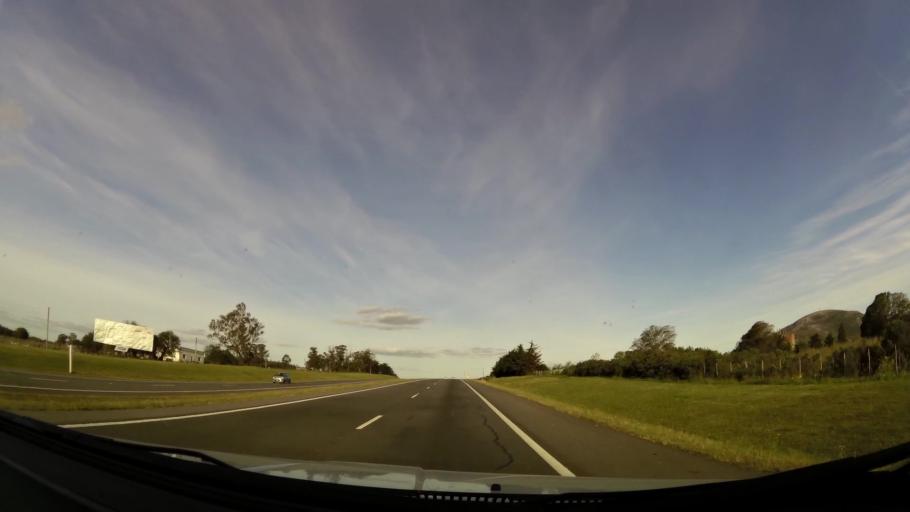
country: UY
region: Maldonado
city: Pan de Azucar
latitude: -34.7885
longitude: -55.2918
